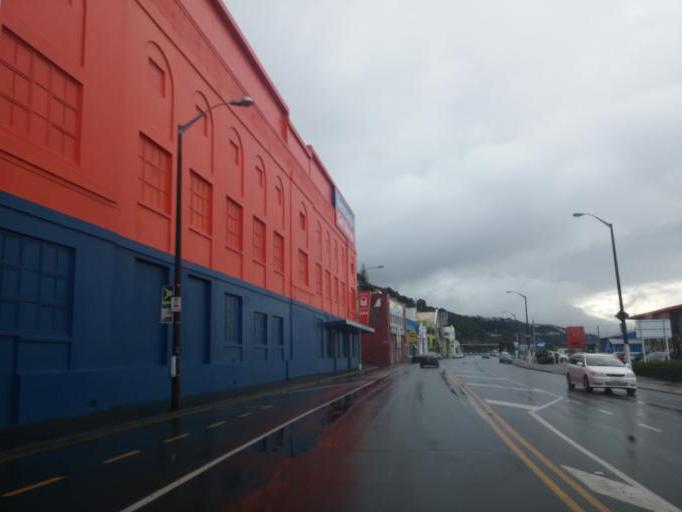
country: NZ
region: Wellington
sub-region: Wellington City
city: Wellington
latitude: -41.2673
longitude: 174.7815
